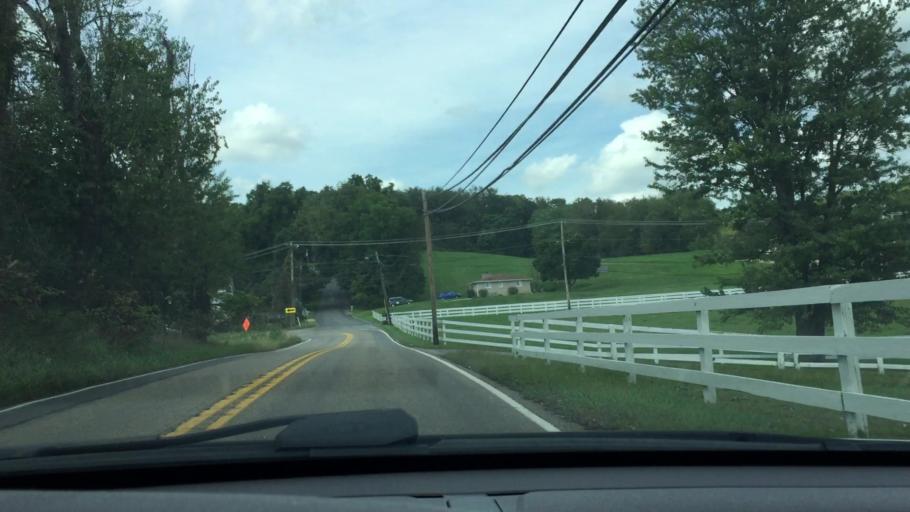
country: US
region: Pennsylvania
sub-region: Washington County
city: Thompsonville
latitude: 40.3072
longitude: -80.1357
